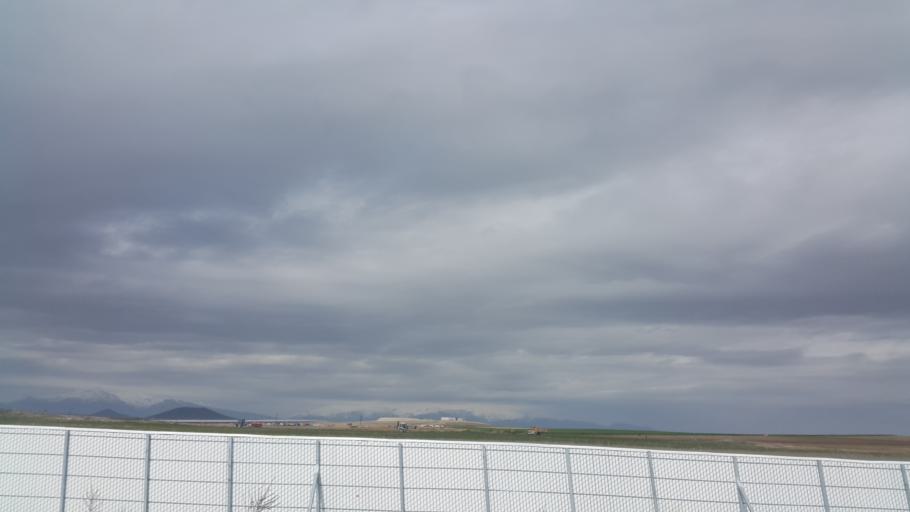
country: TR
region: Nigde
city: Altunhisar
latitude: 37.8650
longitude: 34.1627
